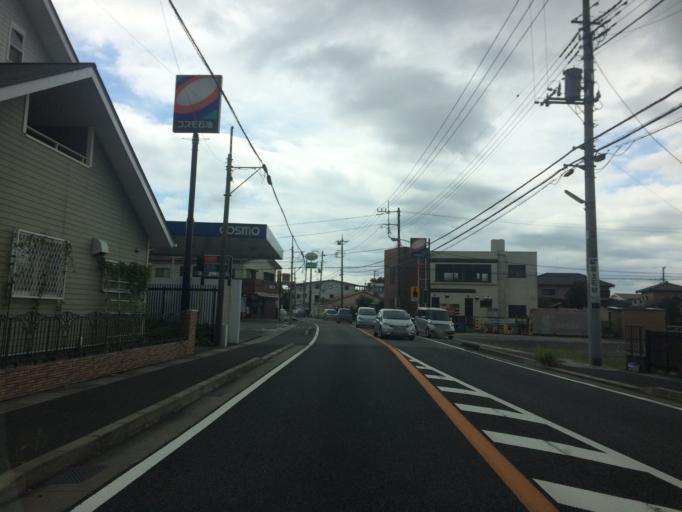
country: JP
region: Shizuoka
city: Fuji
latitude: 35.1659
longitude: 138.6492
